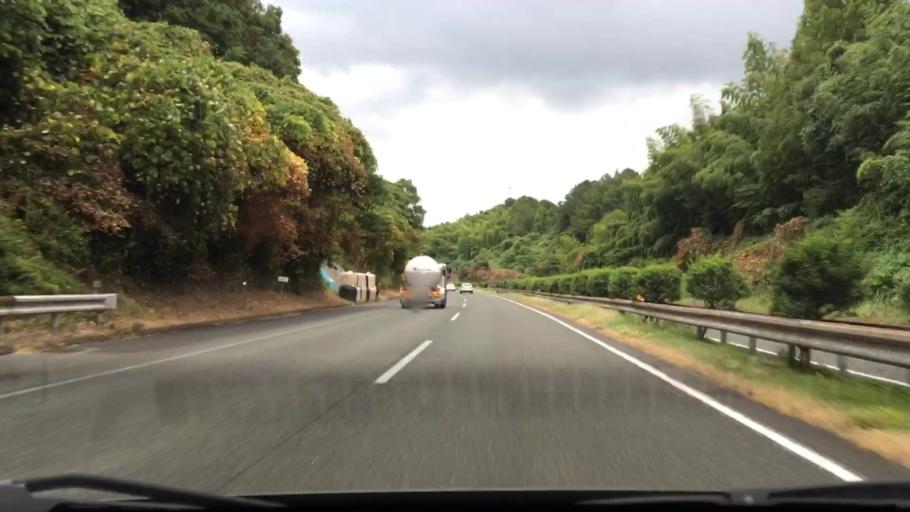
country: JP
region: Fukuoka
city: Miyata
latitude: 33.7472
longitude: 130.5949
